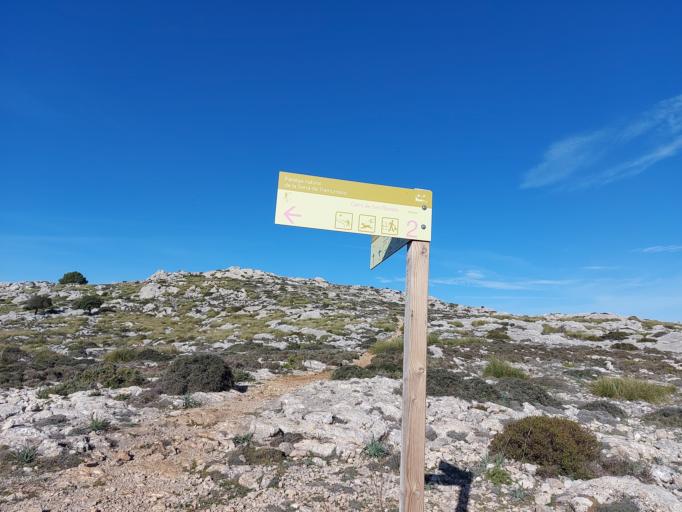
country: ES
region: Balearic Islands
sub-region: Illes Balears
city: Deia
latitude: 39.7283
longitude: 2.6386
